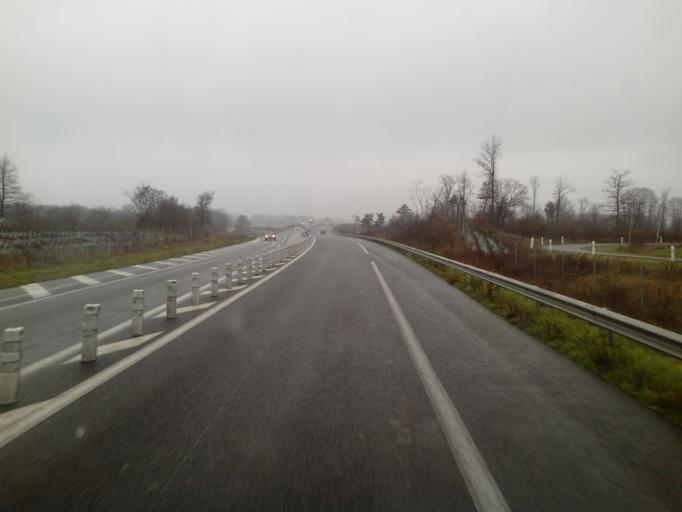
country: FR
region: Poitou-Charentes
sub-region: Departement de la Vienne
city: Terce
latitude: 46.4584
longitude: 0.5552
